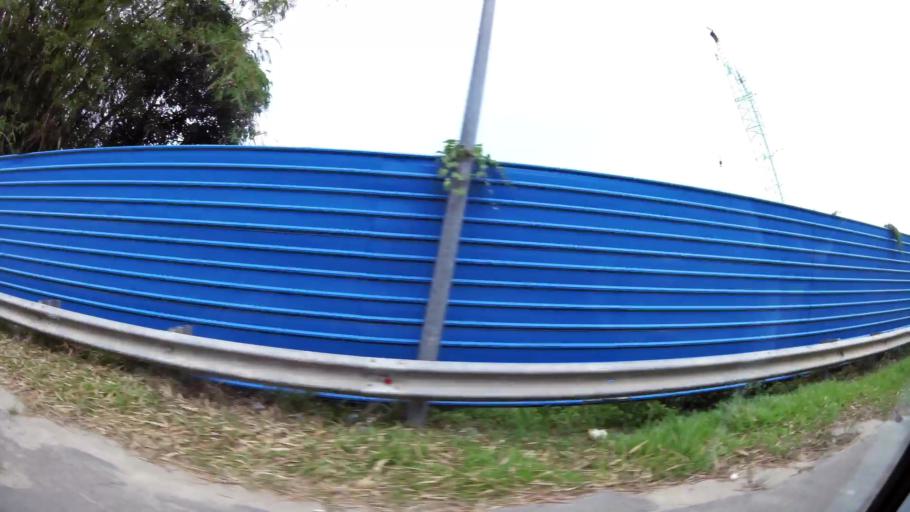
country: BN
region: Brunei and Muara
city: Bandar Seri Begawan
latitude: 4.9278
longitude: 115.0142
